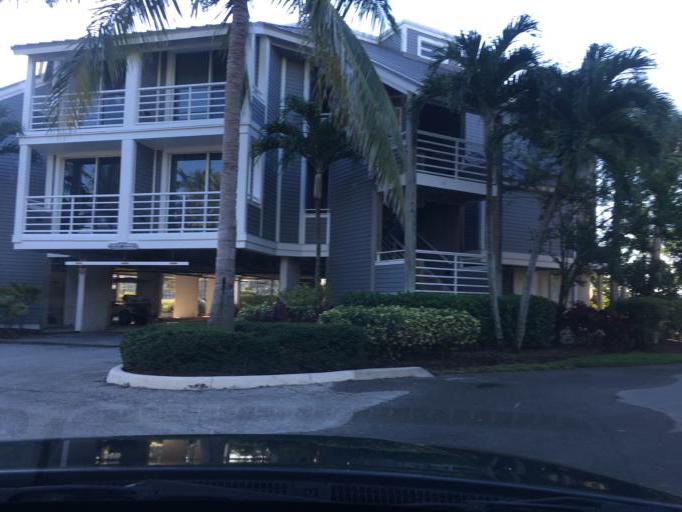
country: US
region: Florida
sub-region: Lee County
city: Pine Island Center
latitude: 26.5516
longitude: -82.1999
